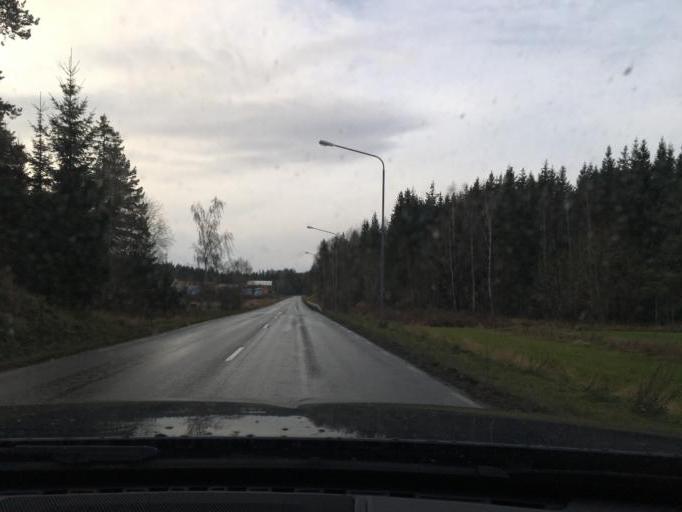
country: SE
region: Joenkoeping
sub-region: Jonkopings Kommun
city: Kaxholmen
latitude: 57.9226
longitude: 14.3938
